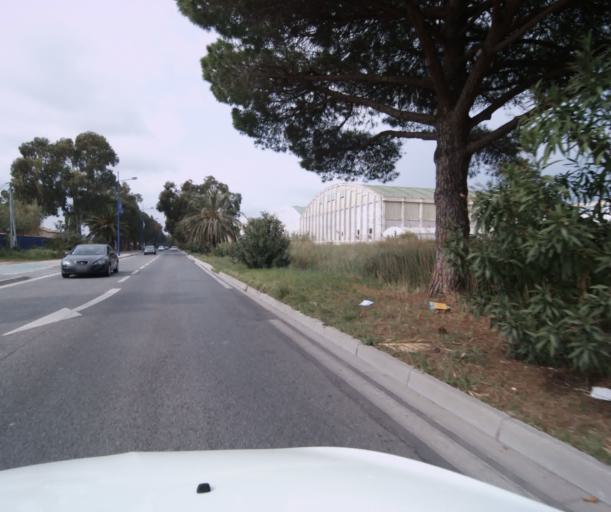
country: FR
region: Provence-Alpes-Cote d'Azur
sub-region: Departement du Var
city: Hyeres
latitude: 43.0883
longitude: 6.1451
